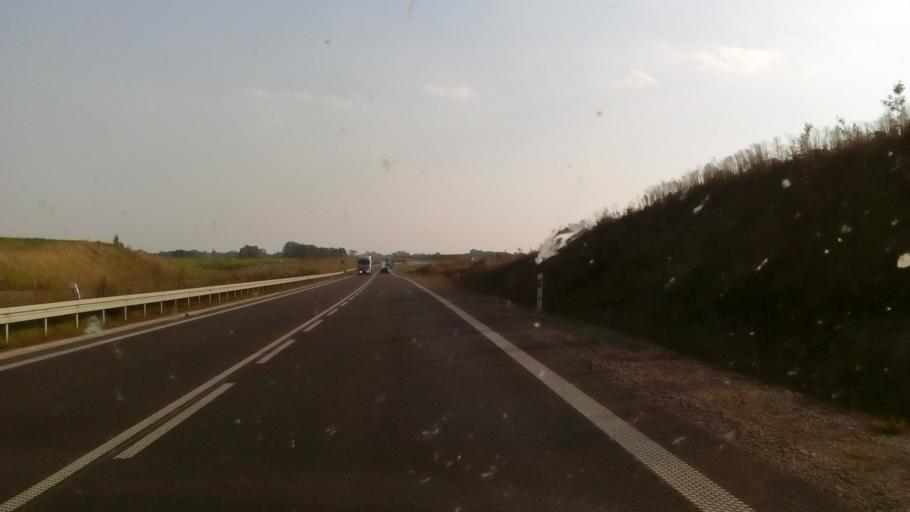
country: PL
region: Podlasie
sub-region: Powiat grajewski
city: Rajgrod
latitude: 53.7730
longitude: 22.8342
